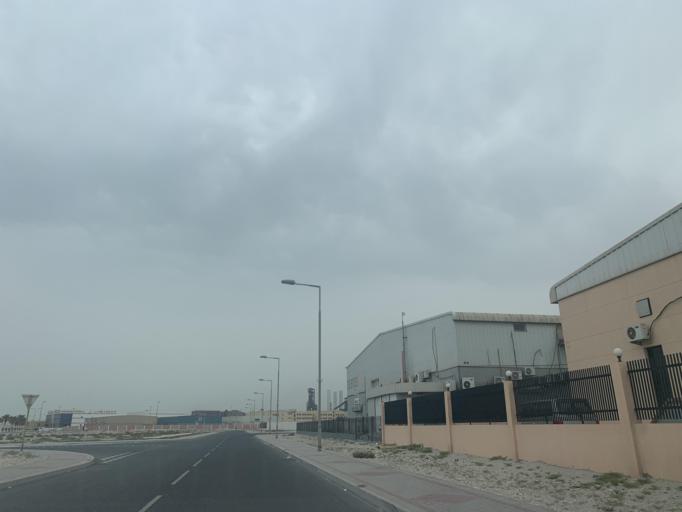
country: BH
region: Muharraq
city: Al Hadd
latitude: 26.2129
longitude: 50.6814
